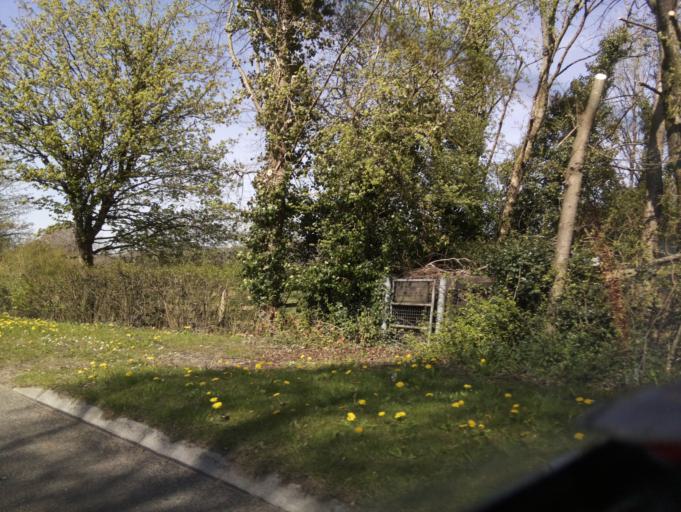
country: GB
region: Wales
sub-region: Rhondda Cynon Taf
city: Aberdare
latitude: 51.7071
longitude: -3.4315
